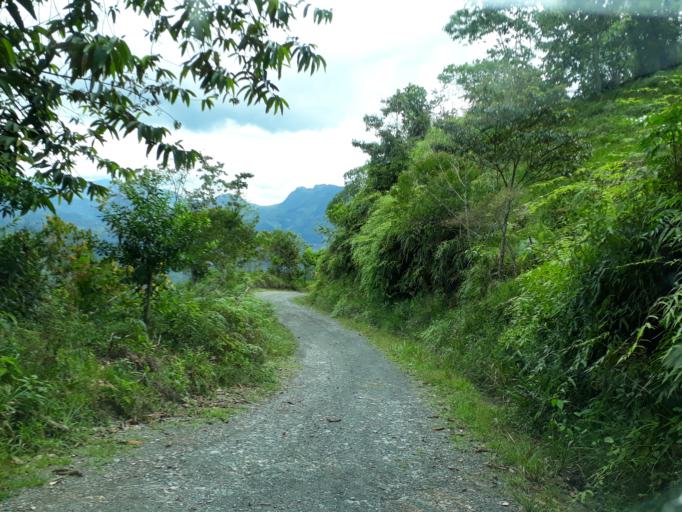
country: CO
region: Boyaca
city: Quipama
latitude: 5.3945
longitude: -74.1250
